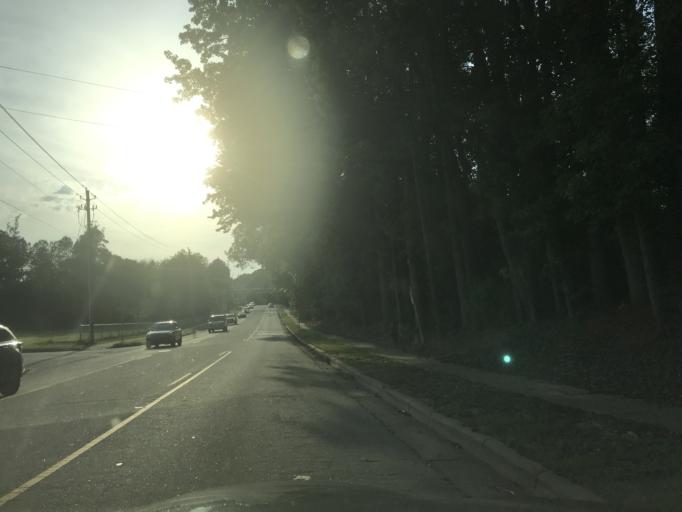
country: US
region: North Carolina
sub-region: Wake County
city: Raleigh
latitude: 35.7419
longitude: -78.6367
